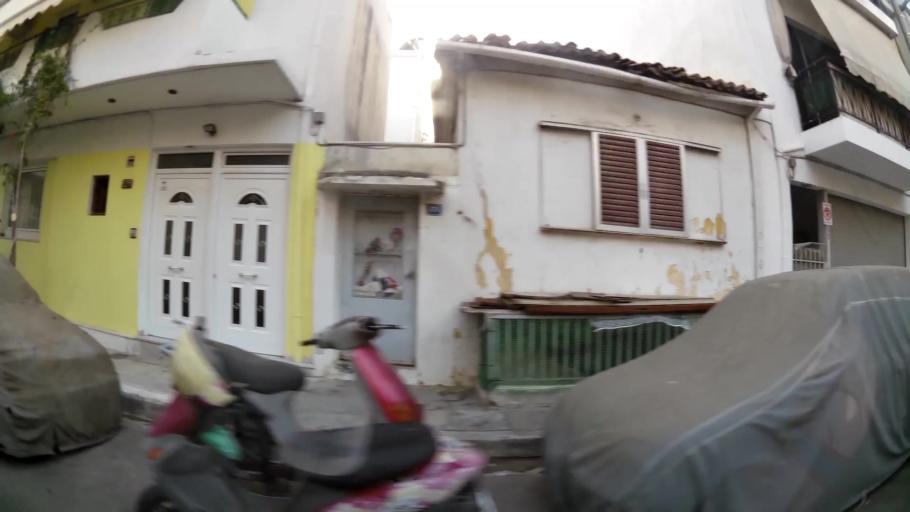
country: GR
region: Attica
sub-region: Nomos Piraios
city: Nikaia
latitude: 37.9748
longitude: 23.6440
